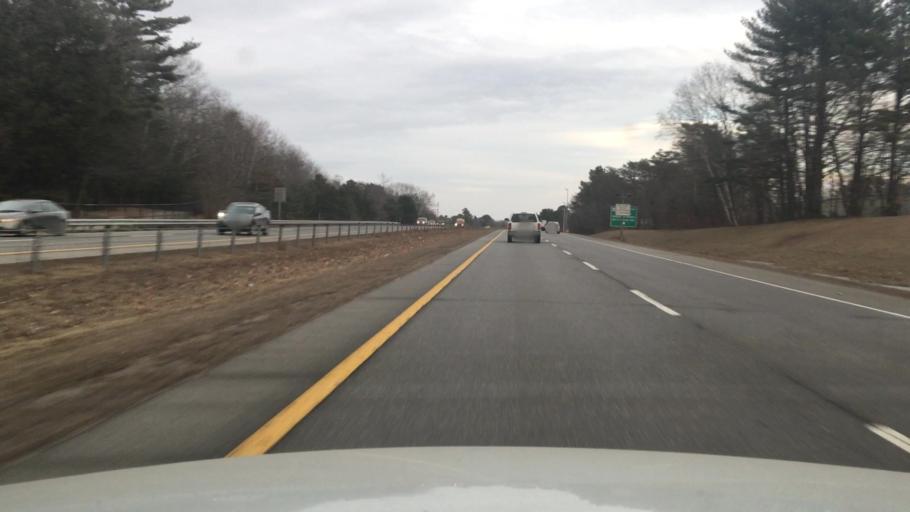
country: US
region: Maine
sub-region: Cumberland County
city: Brunswick
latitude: 43.9092
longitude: -69.9233
